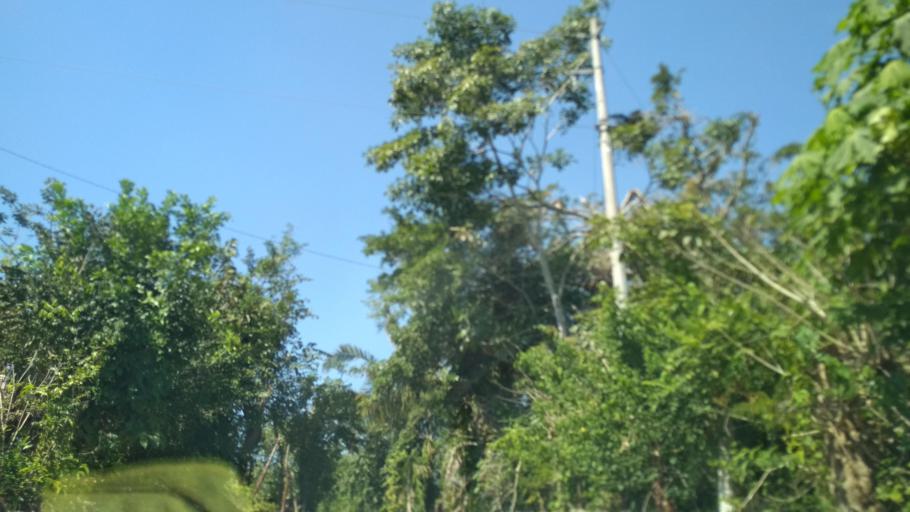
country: MX
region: Veracruz
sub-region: Papantla
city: Polutla
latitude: 20.4817
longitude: -97.2242
